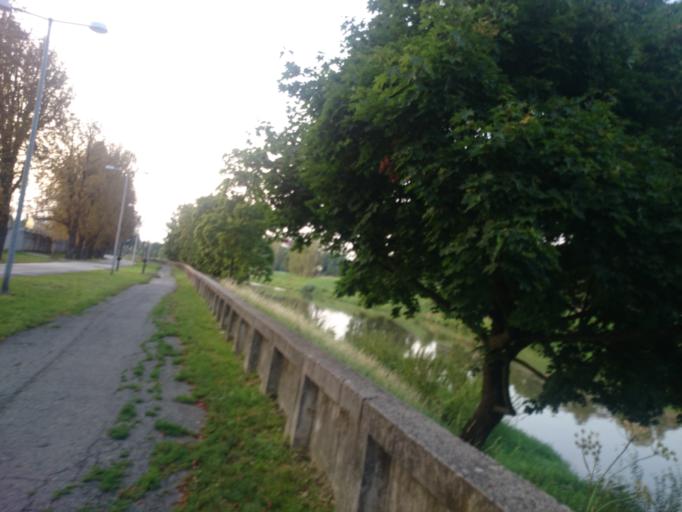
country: CZ
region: Olomoucky
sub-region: Okres Olomouc
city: Olomouc
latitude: 49.5998
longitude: 17.2662
